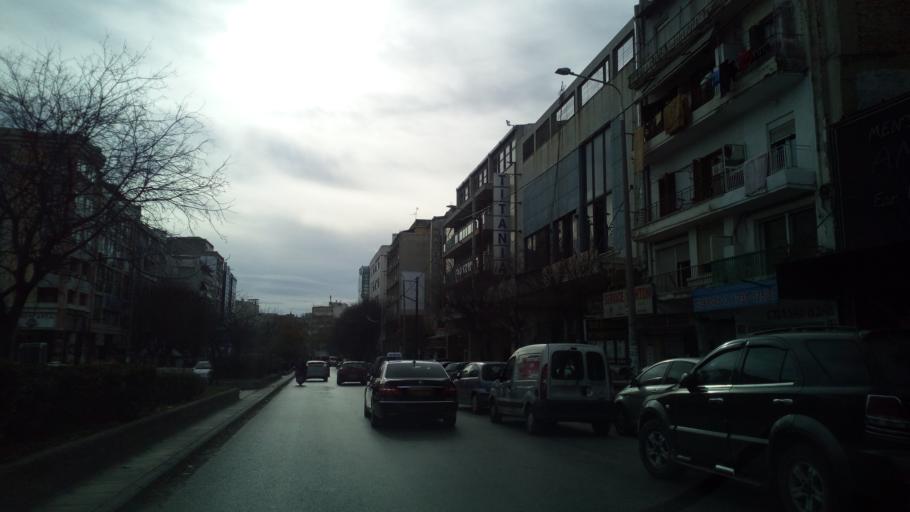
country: GR
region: Central Macedonia
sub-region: Nomos Thessalonikis
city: Thessaloniki
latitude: 40.6434
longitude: 22.9352
